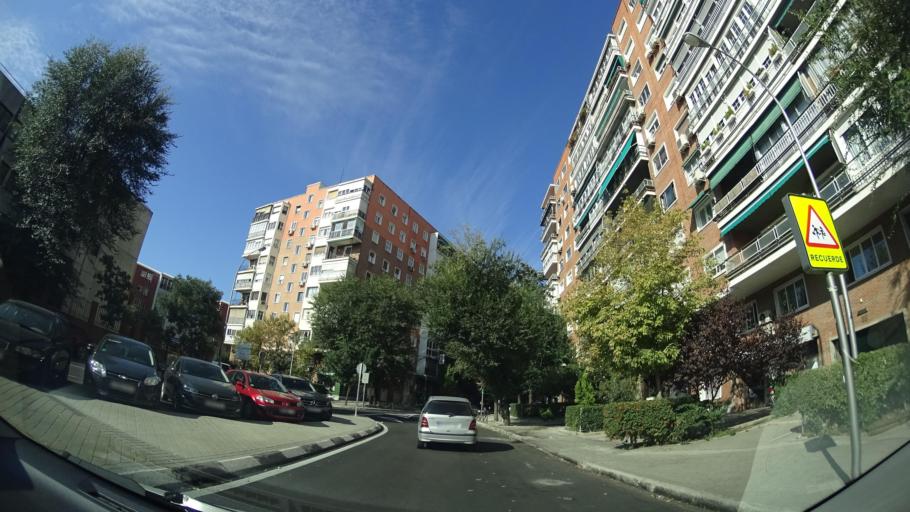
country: ES
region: Madrid
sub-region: Provincia de Madrid
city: Salamanca
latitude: 40.4385
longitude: -3.6615
